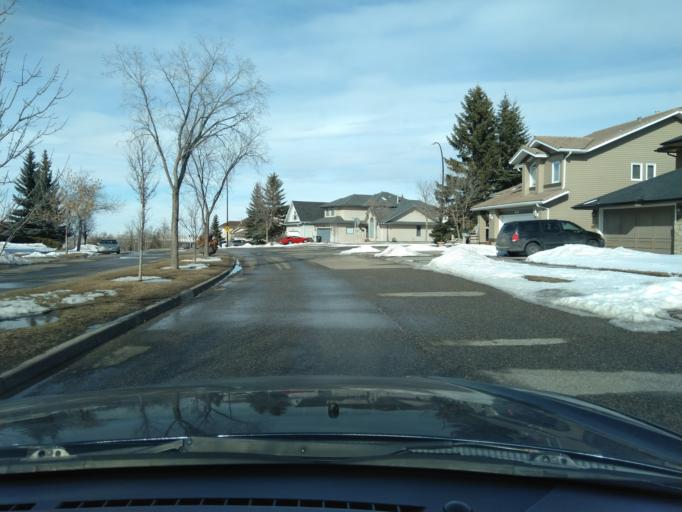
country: CA
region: Alberta
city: Calgary
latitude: 51.1309
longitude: -114.1348
